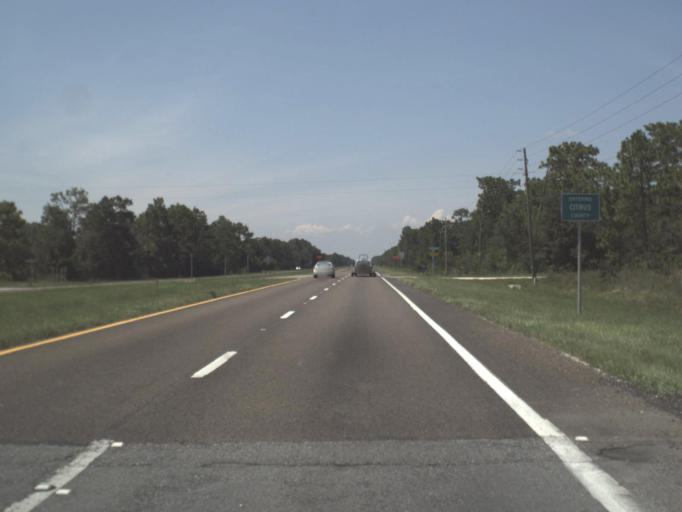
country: US
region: Florida
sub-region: Citrus County
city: Sugarmill Woods
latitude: 28.6946
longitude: -82.5524
